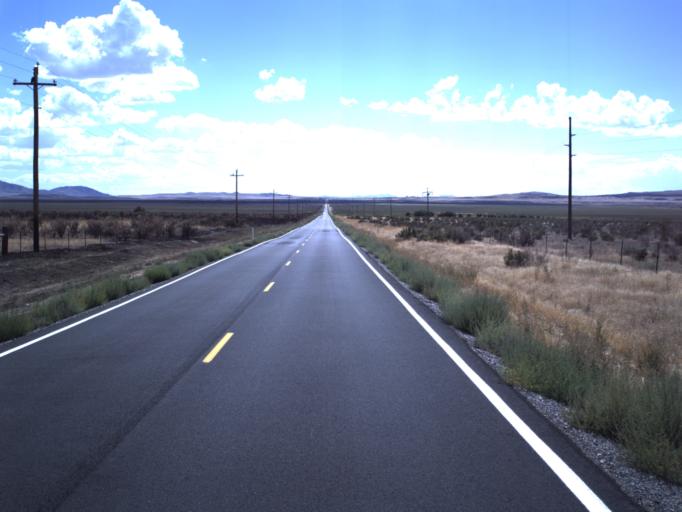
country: US
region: Utah
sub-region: Tooele County
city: Grantsville
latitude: 40.2914
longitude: -112.6588
